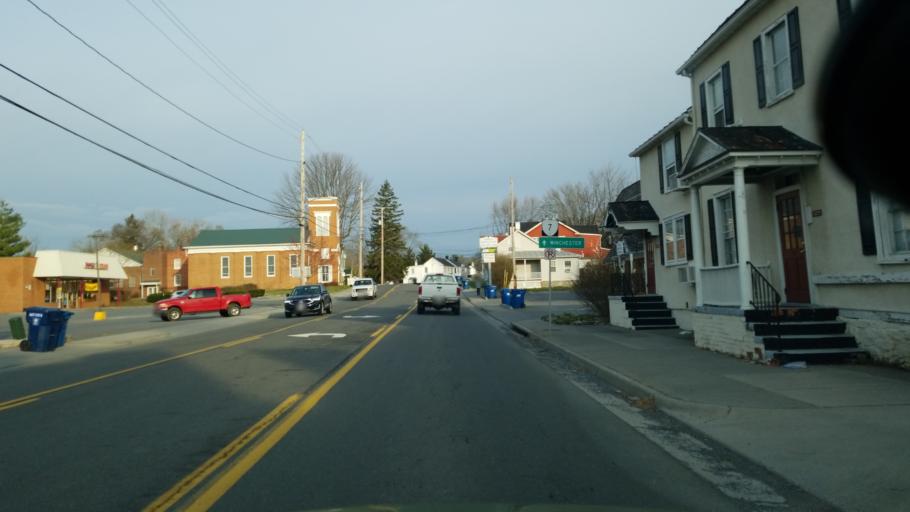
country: US
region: Virginia
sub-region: Clarke County
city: Berryville
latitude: 39.1520
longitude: -77.9831
